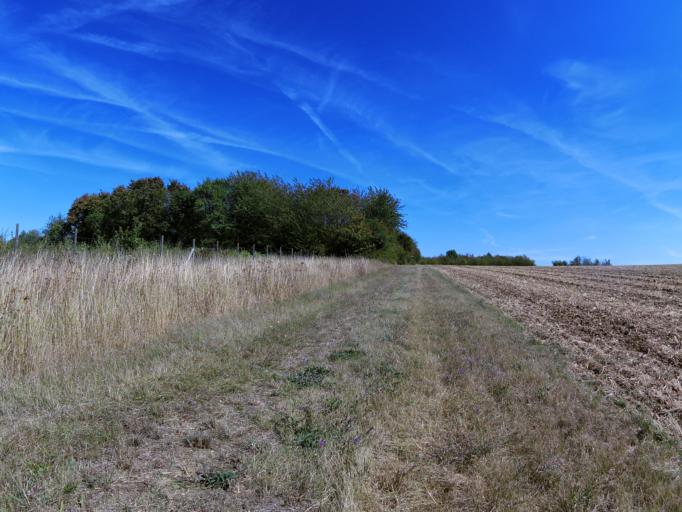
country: DE
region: Bavaria
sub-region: Regierungsbezirk Unterfranken
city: Guntersleben
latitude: 49.8713
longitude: 9.8827
